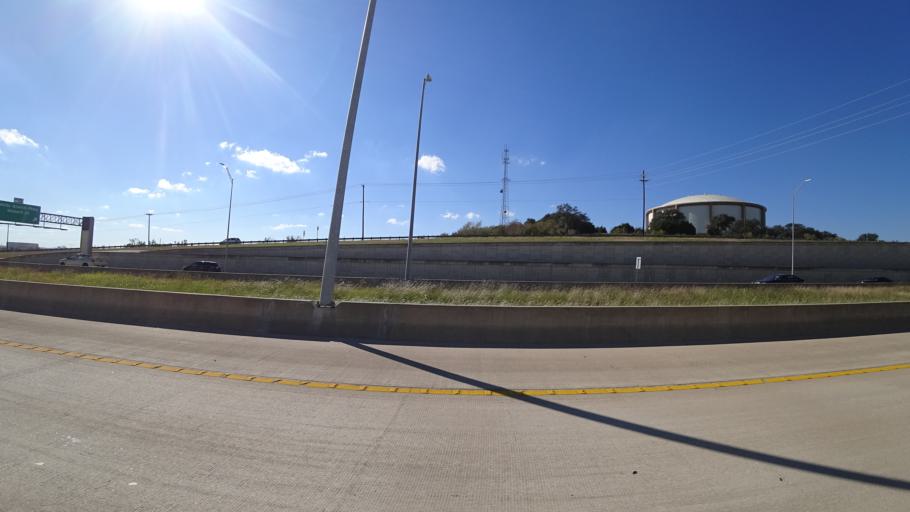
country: US
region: Texas
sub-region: Travis County
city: Wells Branch
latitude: 30.4589
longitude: -97.6985
